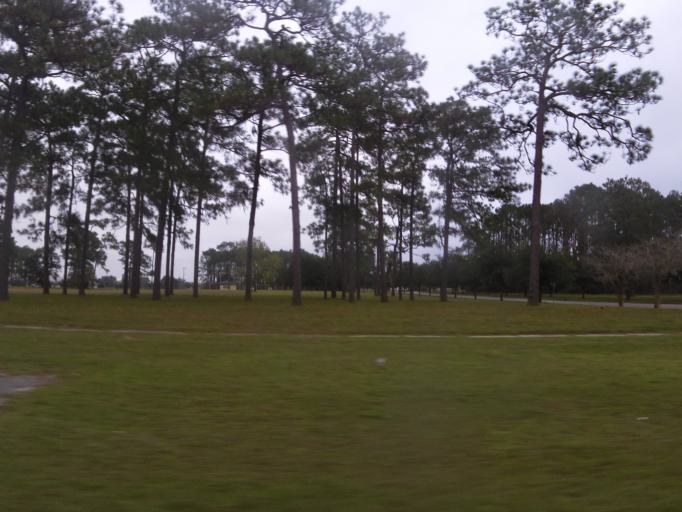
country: US
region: Florida
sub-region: Duval County
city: Baldwin
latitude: 30.2258
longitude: -81.8895
